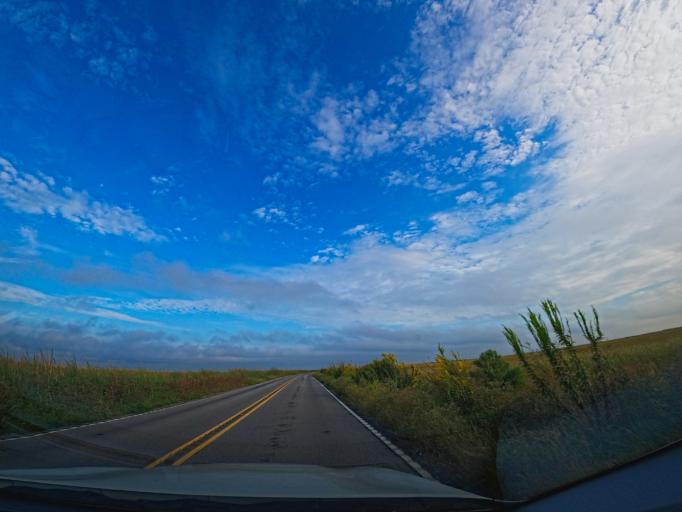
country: US
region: Louisiana
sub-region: Terrebonne Parish
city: Dulac
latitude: 29.3145
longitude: -90.6774
